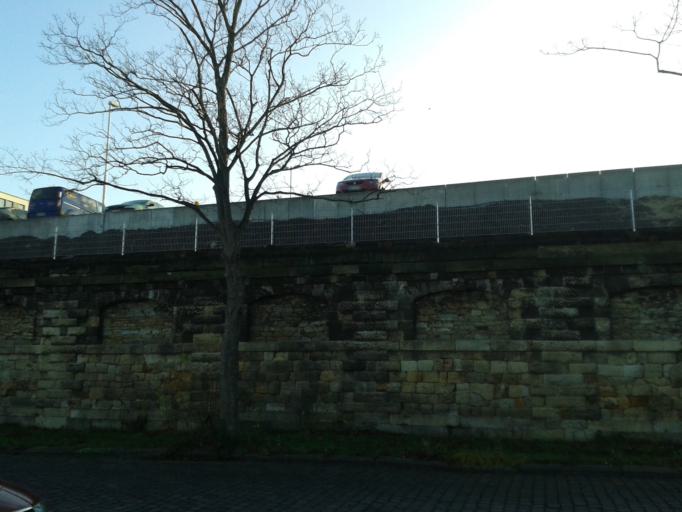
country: DE
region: Saxony
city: Dresden
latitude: 51.0407
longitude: 13.7165
